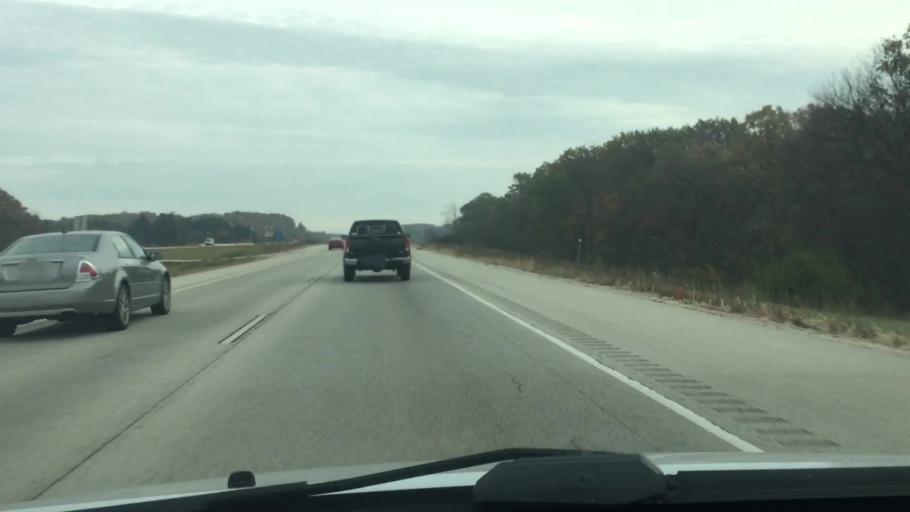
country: US
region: Wisconsin
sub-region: Waukesha County
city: Mukwonago
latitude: 42.8719
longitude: -88.2901
